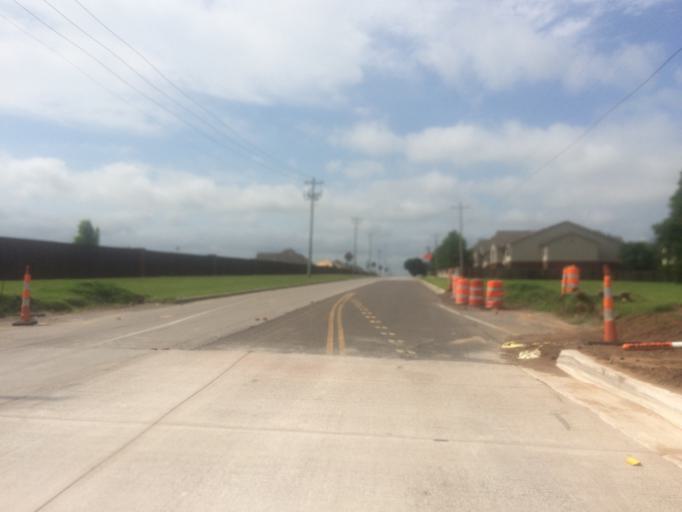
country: US
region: Oklahoma
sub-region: Cleveland County
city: Noble
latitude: 35.1738
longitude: -97.4237
